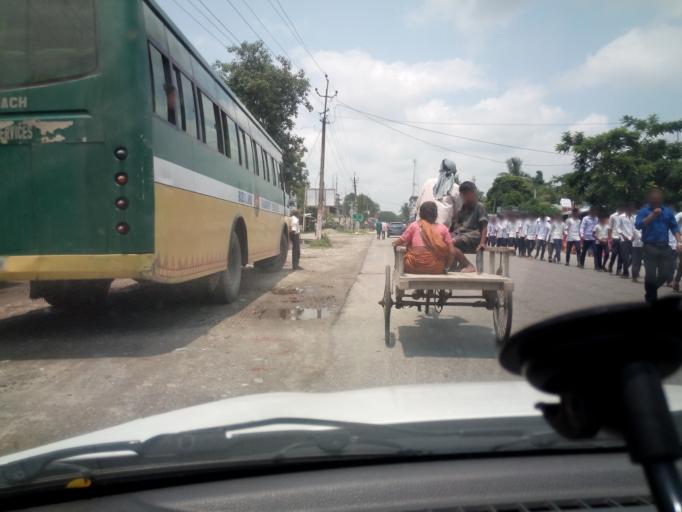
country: IN
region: Assam
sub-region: Udalguri
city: Udalguri
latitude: 26.7097
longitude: 92.2043
